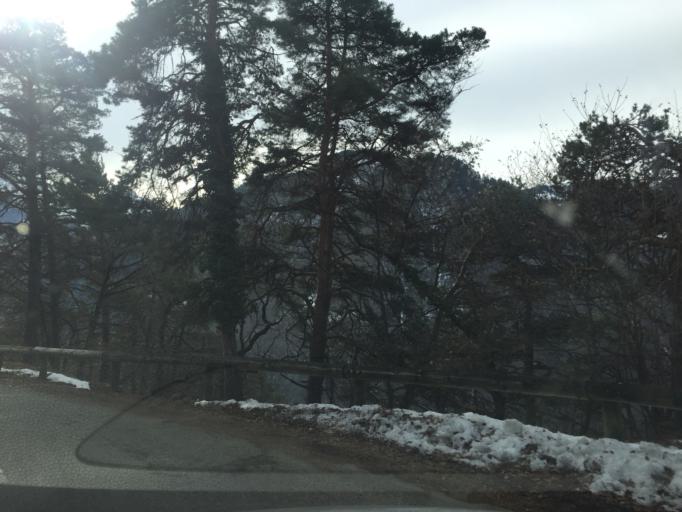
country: FR
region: Rhone-Alpes
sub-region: Departement de la Savoie
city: Aigueblanche
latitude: 45.5273
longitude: 6.4866
